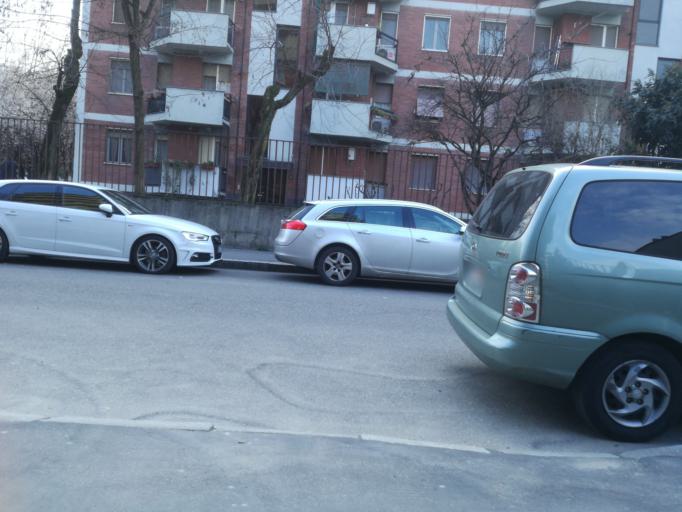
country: IT
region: Lombardy
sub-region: Citta metropolitana di Milano
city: Romano Banco
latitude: 45.4568
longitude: 9.1211
